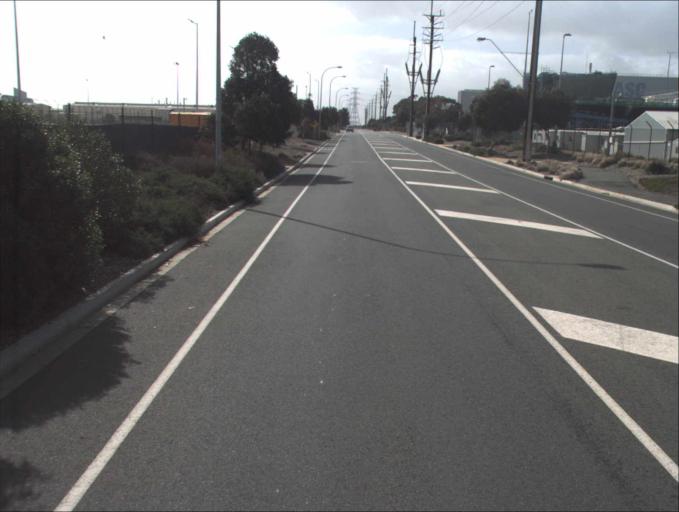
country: AU
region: South Australia
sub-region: Port Adelaide Enfield
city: Birkenhead
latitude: -34.7868
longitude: 138.5067
